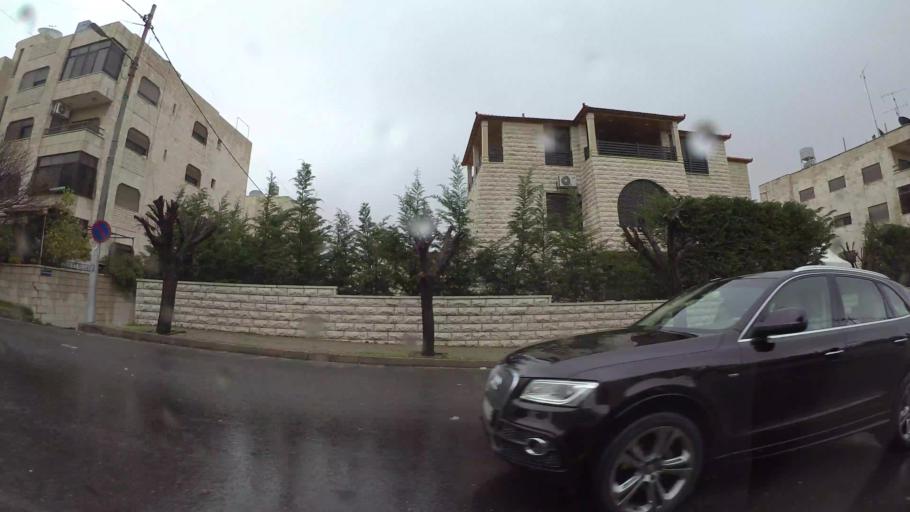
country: JO
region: Amman
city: Wadi as Sir
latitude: 31.9669
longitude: 35.8526
